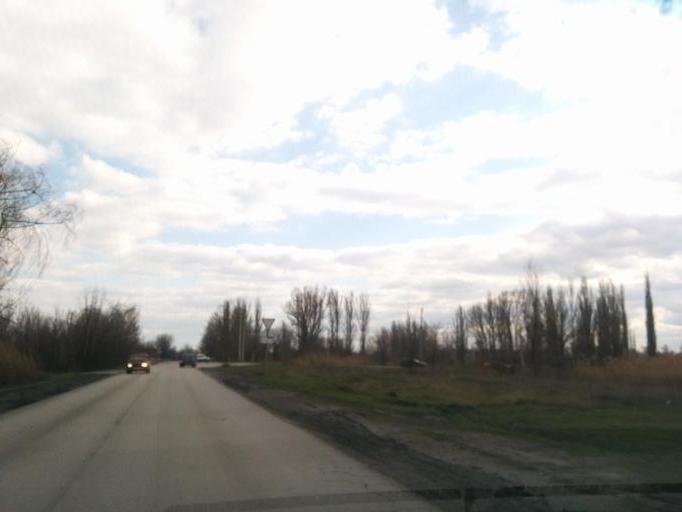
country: RU
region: Rostov
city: Shakhty
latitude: 47.6798
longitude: 40.2853
